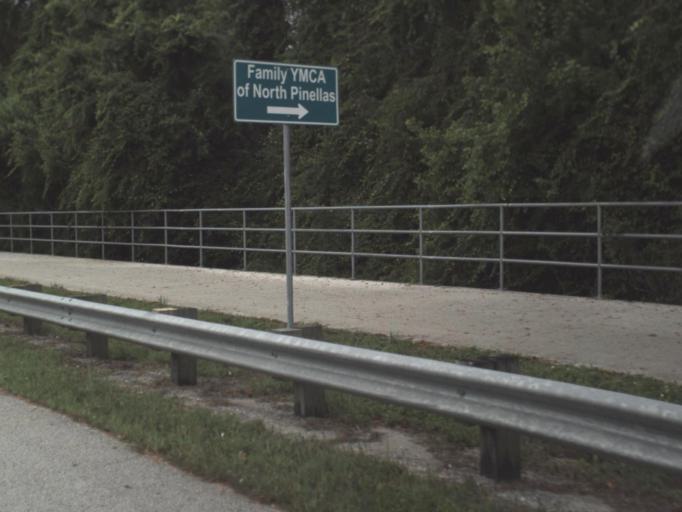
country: US
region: Florida
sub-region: Pinellas County
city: East Lake
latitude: 28.1029
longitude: -82.6944
